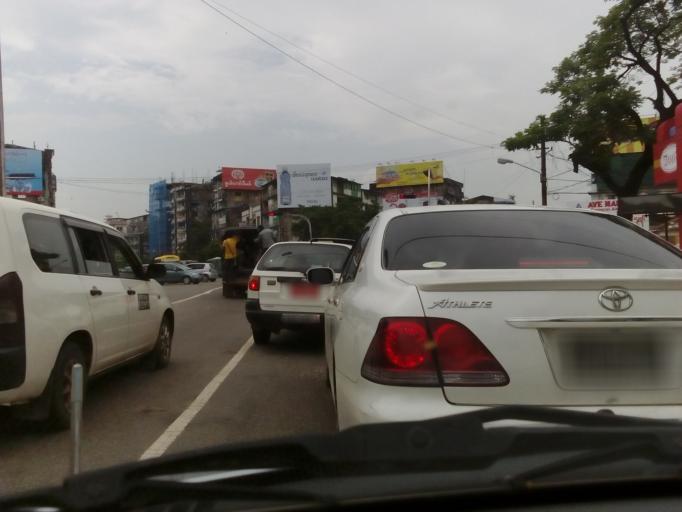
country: MM
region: Yangon
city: Yangon
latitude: 16.8110
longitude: 96.1712
